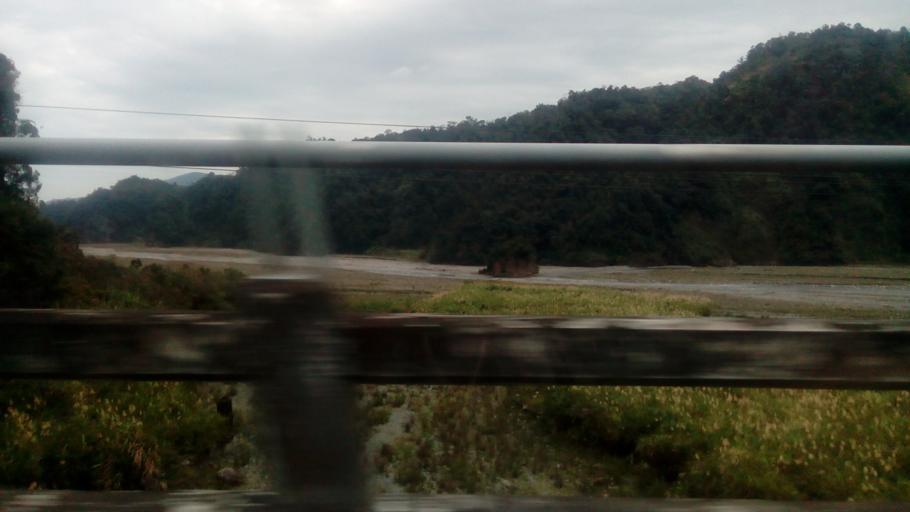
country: TW
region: Taiwan
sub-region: Yilan
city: Yilan
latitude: 24.6382
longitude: 121.5539
